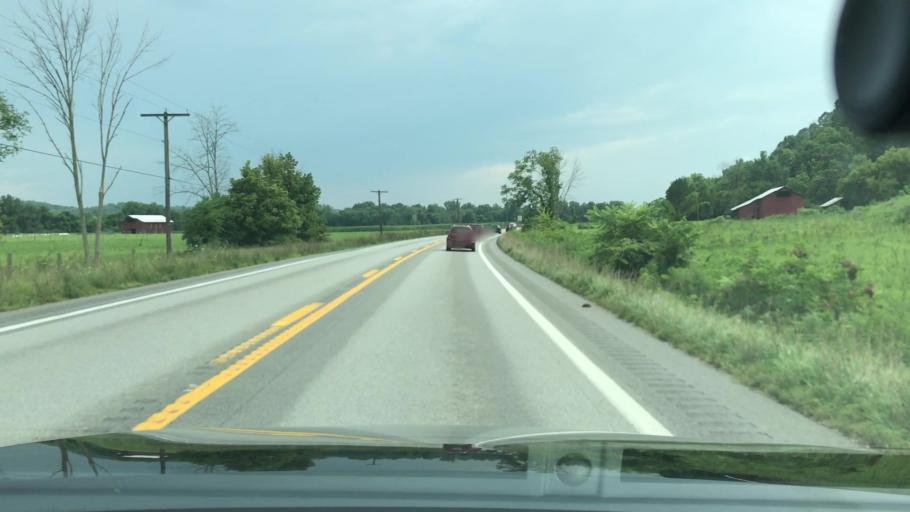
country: US
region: West Virginia
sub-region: Putnam County
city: Buffalo
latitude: 38.6325
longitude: -81.9786
